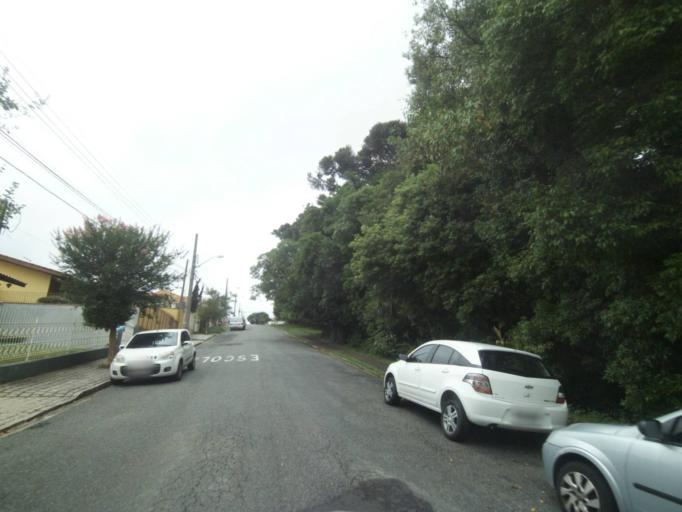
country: BR
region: Parana
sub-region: Curitiba
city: Curitiba
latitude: -25.4277
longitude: -49.3437
